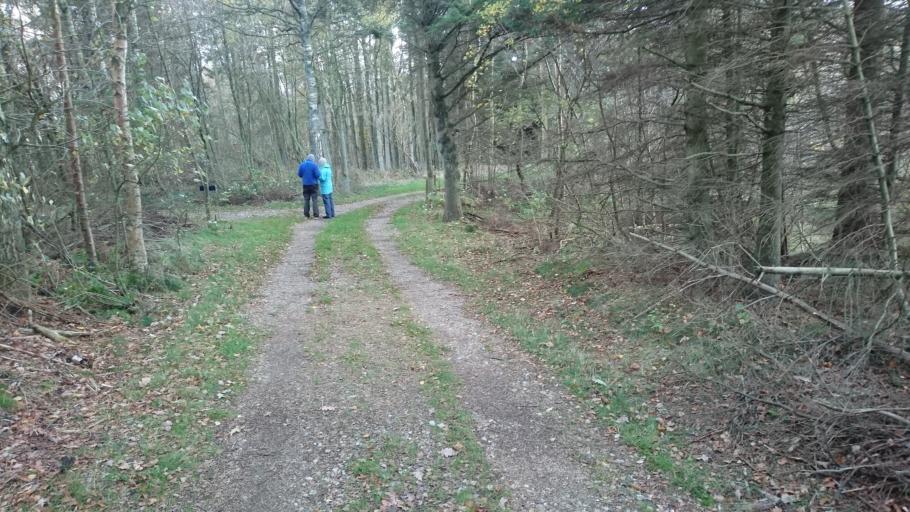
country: DK
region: North Denmark
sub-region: Morso Kommune
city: Nykobing Mors
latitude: 56.8374
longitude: 8.9754
